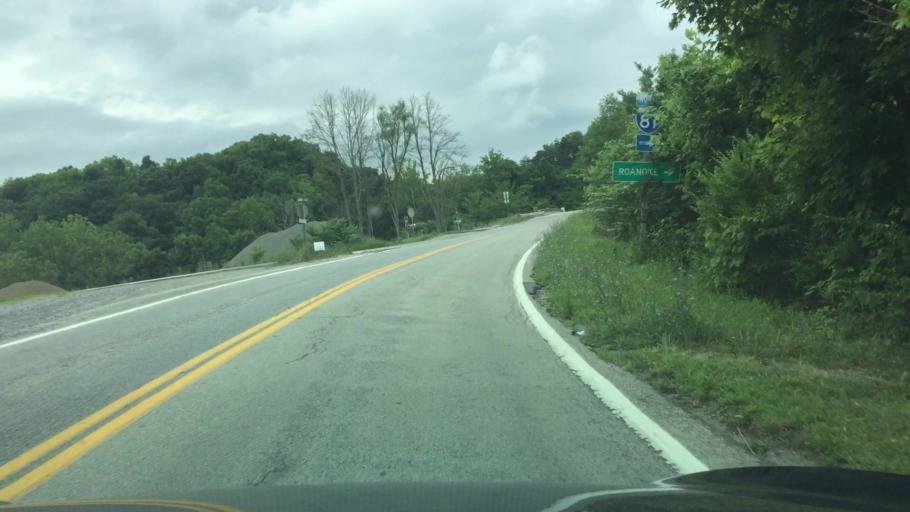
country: US
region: Virginia
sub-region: Pulaski County
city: Pulaski
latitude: 37.0061
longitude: -80.7511
